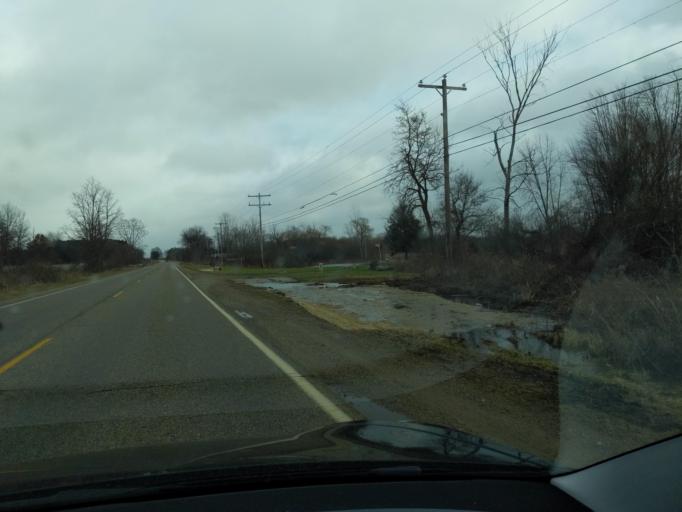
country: US
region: Michigan
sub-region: Jackson County
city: Spring Arbor
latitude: 42.2534
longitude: -84.5063
